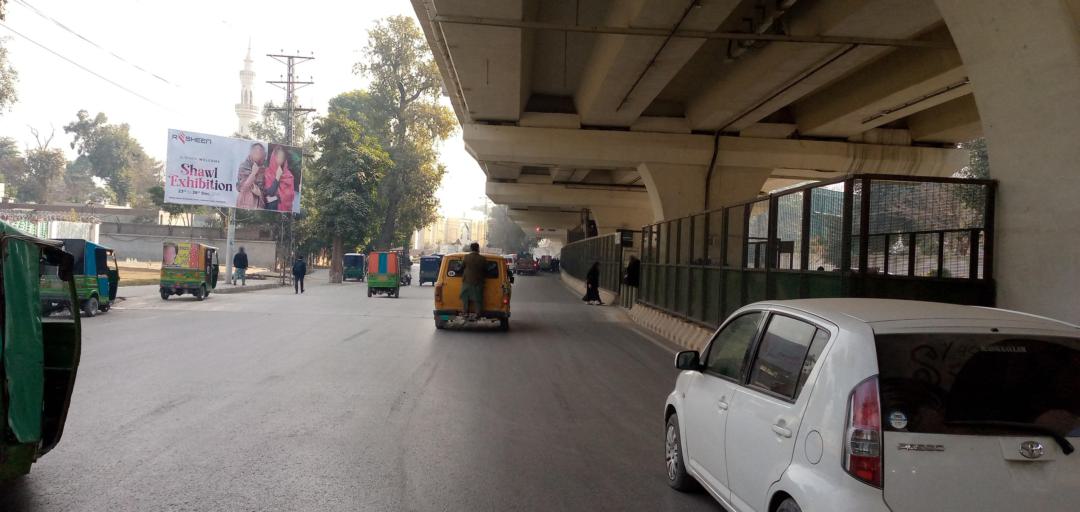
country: PK
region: Khyber Pakhtunkhwa
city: Peshawar
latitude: 33.9991
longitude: 71.5329
